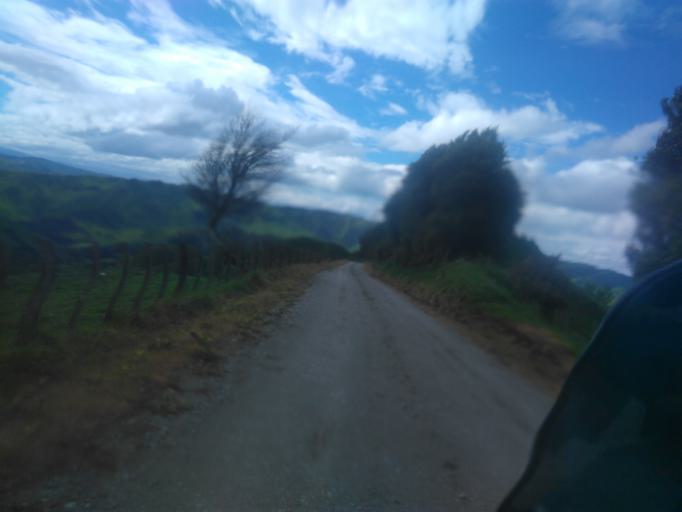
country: NZ
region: Hawke's Bay
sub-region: Wairoa District
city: Wairoa
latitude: -38.7697
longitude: 177.6397
